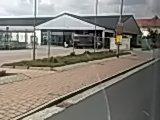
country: DE
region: Saxony
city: Weinbohla
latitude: 51.1588
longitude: 13.5635
